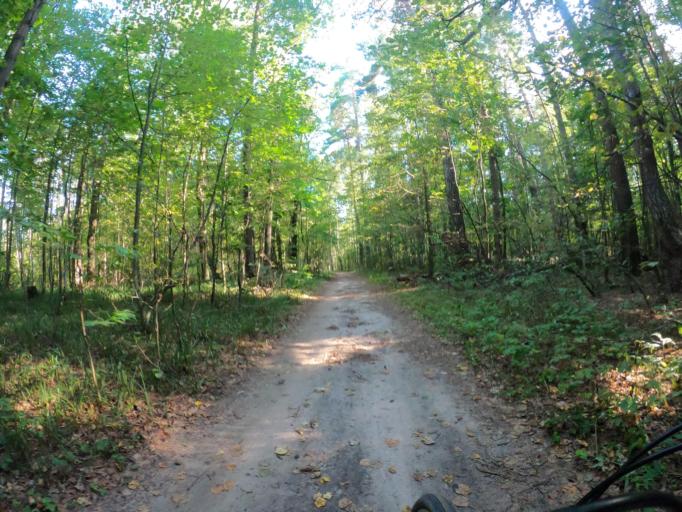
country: RU
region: Moskovskaya
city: Stupino
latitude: 54.8724
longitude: 38.0980
